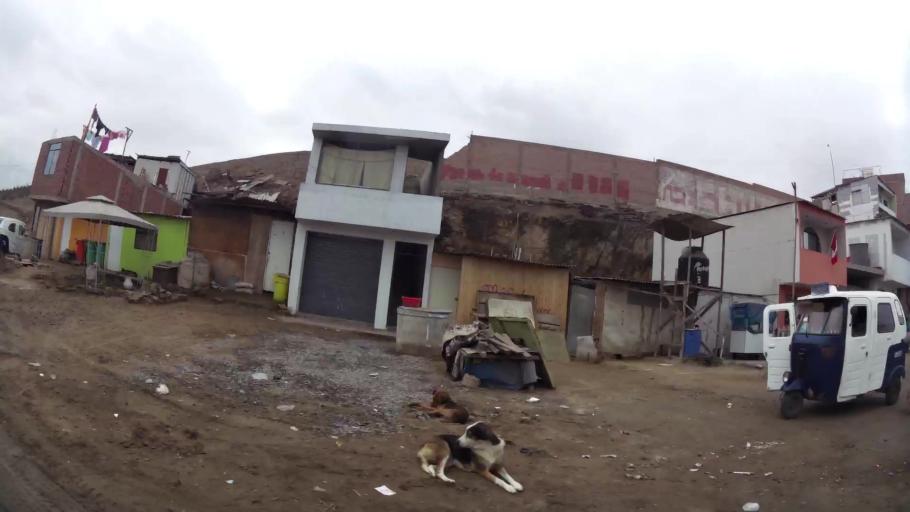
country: PE
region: Lima
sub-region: Lima
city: Surco
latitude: -12.1830
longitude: -76.9915
